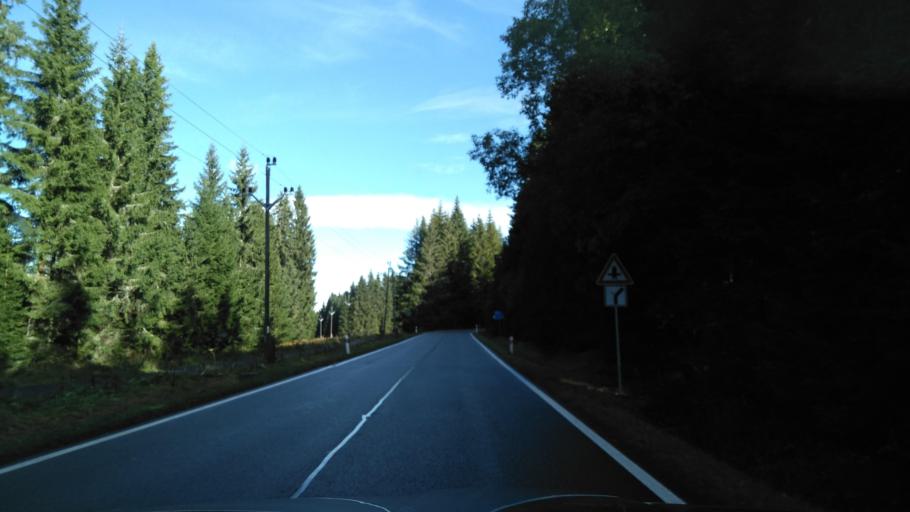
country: CZ
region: Jihocesky
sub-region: Okres Prachatice
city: Borova Lada
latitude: 49.0353
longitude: 13.5773
